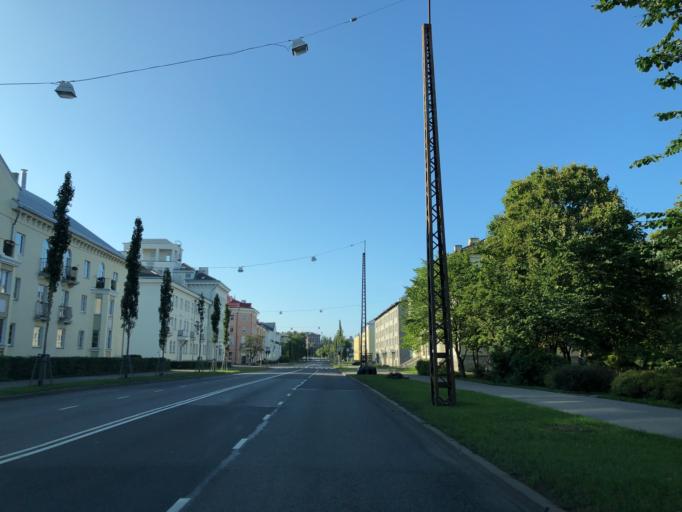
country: EE
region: Harju
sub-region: Tallinna linn
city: Tallinn
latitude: 59.4514
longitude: 24.6949
